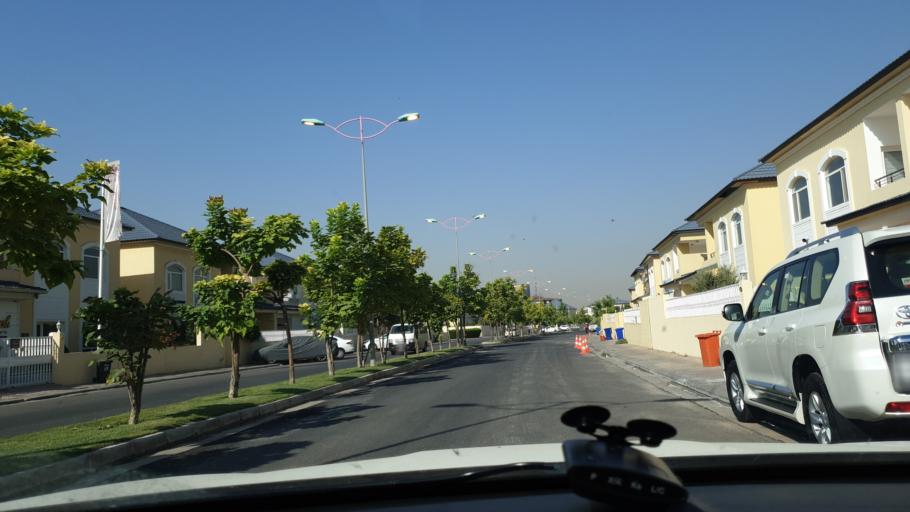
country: IQ
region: Arbil
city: Erbil
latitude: 36.1877
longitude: 43.9675
